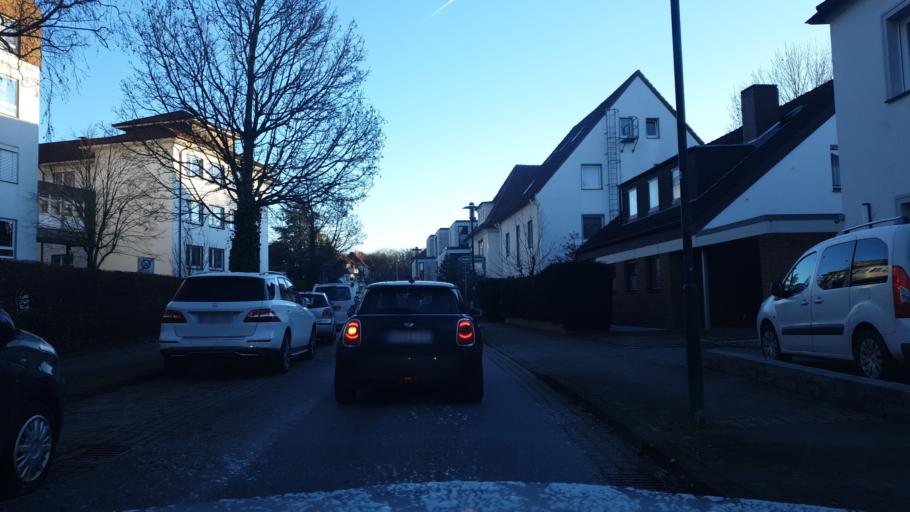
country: DE
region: North Rhine-Westphalia
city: Bad Oeynhausen
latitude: 52.1996
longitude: 8.7875
